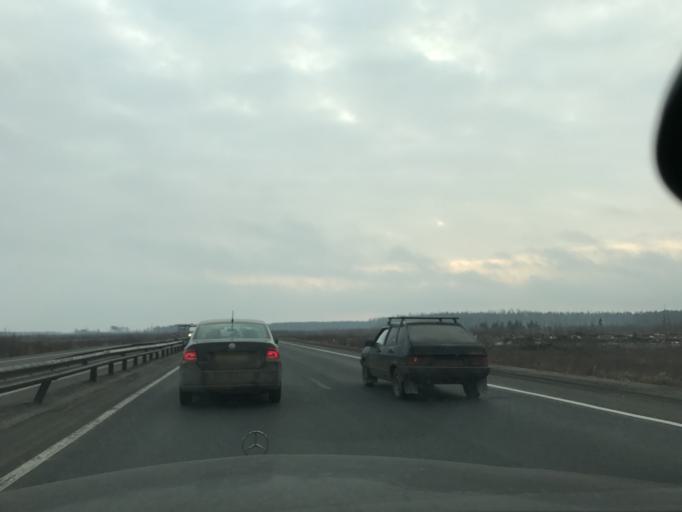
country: RU
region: Moskovskaya
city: Elektrogorsk
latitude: 55.8513
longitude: 38.8227
